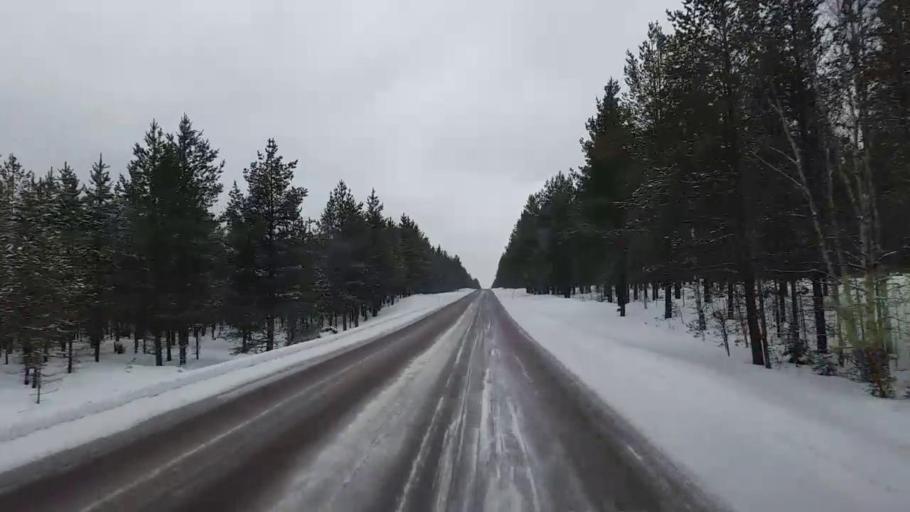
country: SE
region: Jaemtland
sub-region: Bergs Kommun
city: Hoverberg
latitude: 62.4417
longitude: 14.5775
